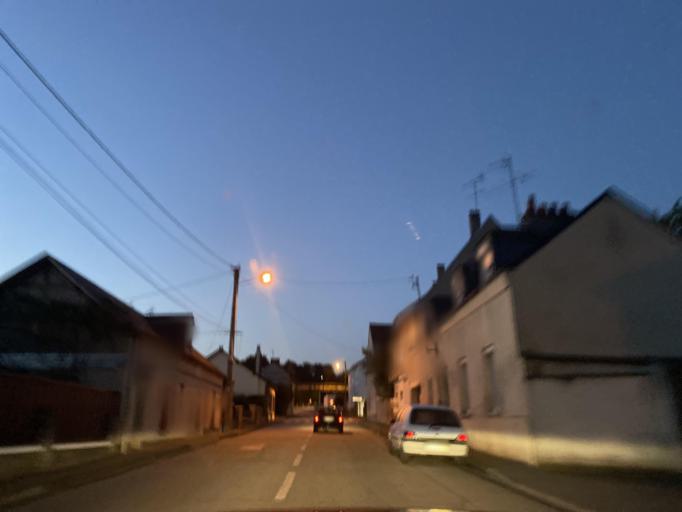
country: FR
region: Haute-Normandie
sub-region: Departement de l'Eure
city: Evreux
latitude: 49.0311
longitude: 1.1599
